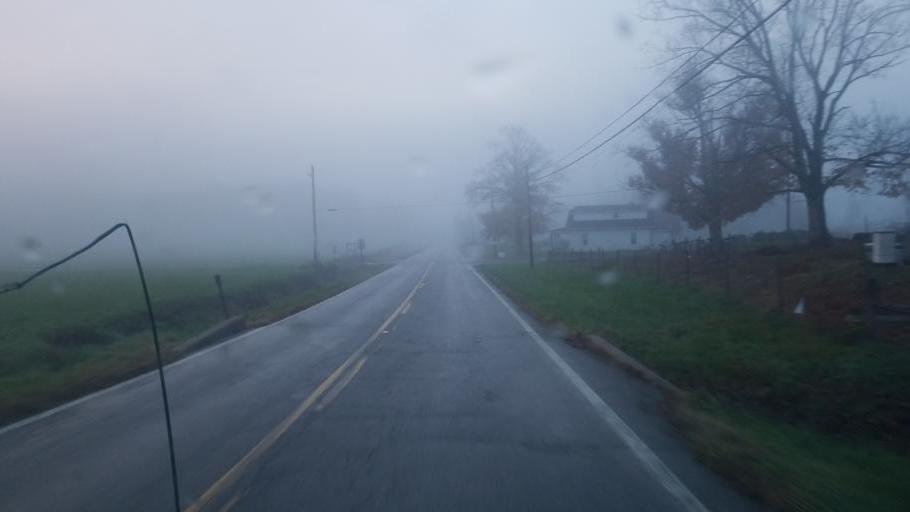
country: US
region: Ohio
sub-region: Morgan County
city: McConnelsville
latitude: 39.5065
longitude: -81.8564
